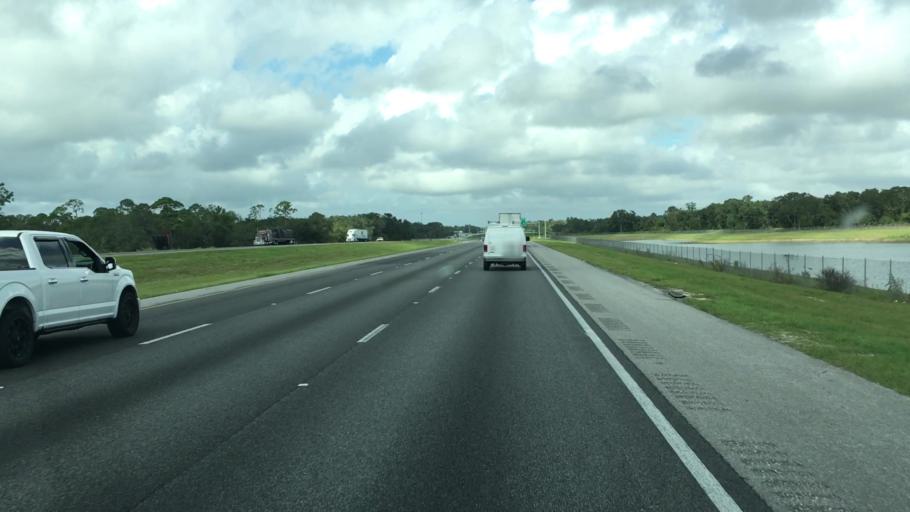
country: US
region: Florida
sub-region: Volusia County
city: Samsula-Spruce Creek
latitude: 29.0841
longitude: -81.0176
